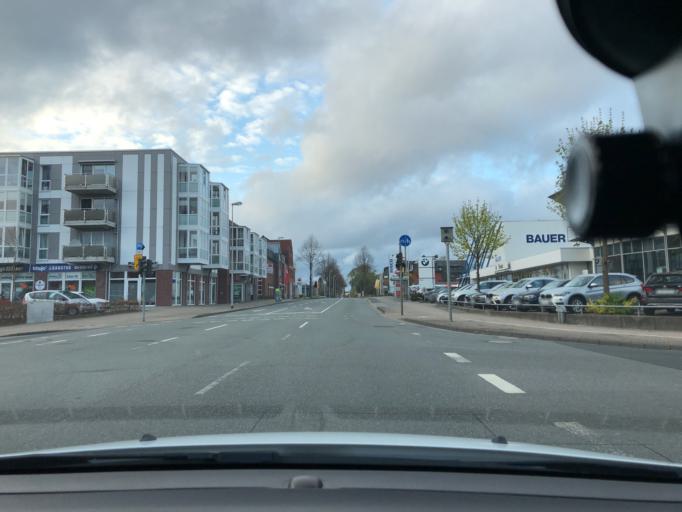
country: DE
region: Schleswig-Holstein
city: Flensburg
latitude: 54.7704
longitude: 9.4352
